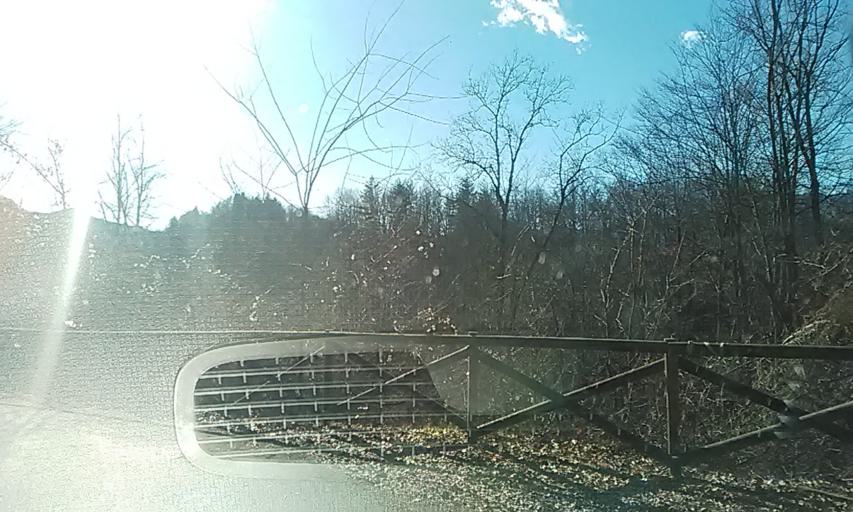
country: IT
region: Piedmont
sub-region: Provincia di Vercelli
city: Valduggia
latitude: 45.7265
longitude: 8.3158
